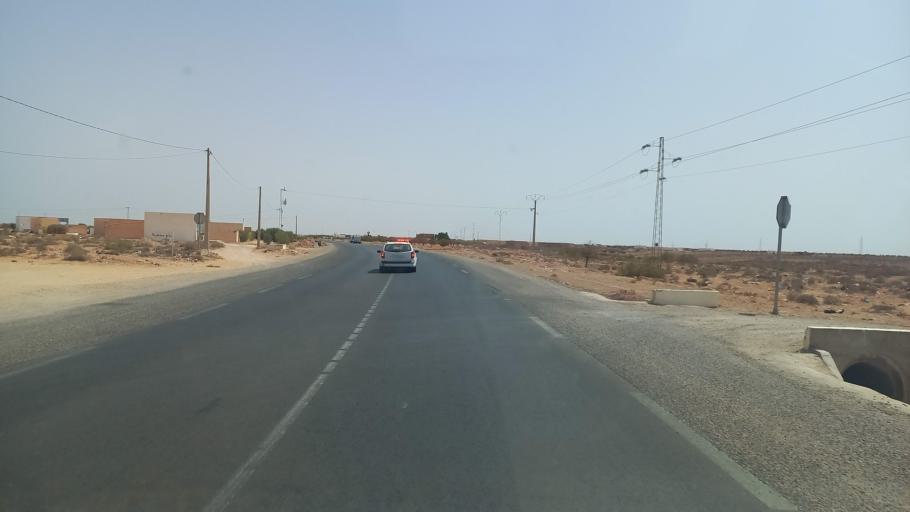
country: TN
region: Madanin
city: Medenine
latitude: 33.3676
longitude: 10.6687
